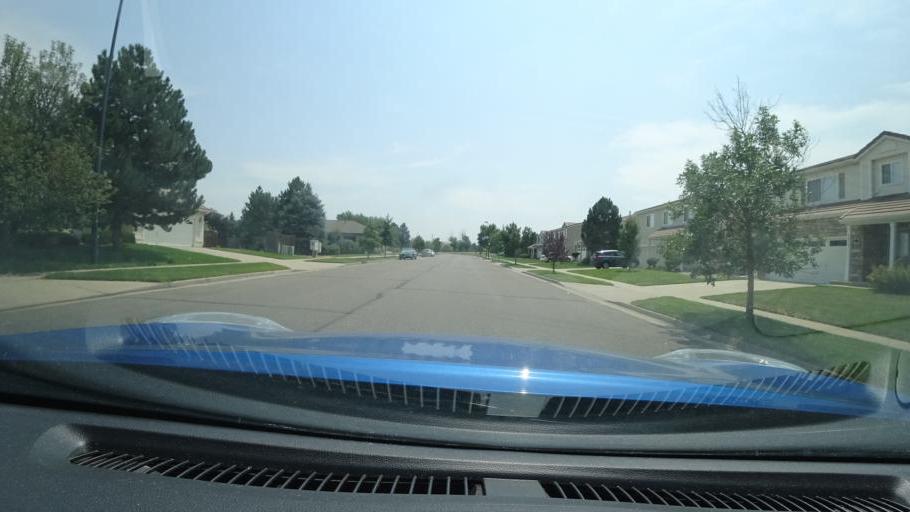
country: US
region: Colorado
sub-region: Adams County
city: Aurora
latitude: 39.7729
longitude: -104.7679
